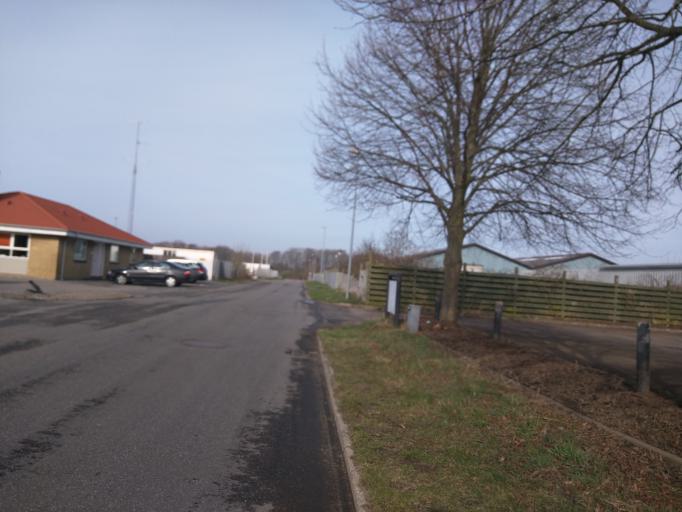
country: DK
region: South Denmark
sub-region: Fredericia Kommune
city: Snoghoj
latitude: 55.5477
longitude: 9.6910
